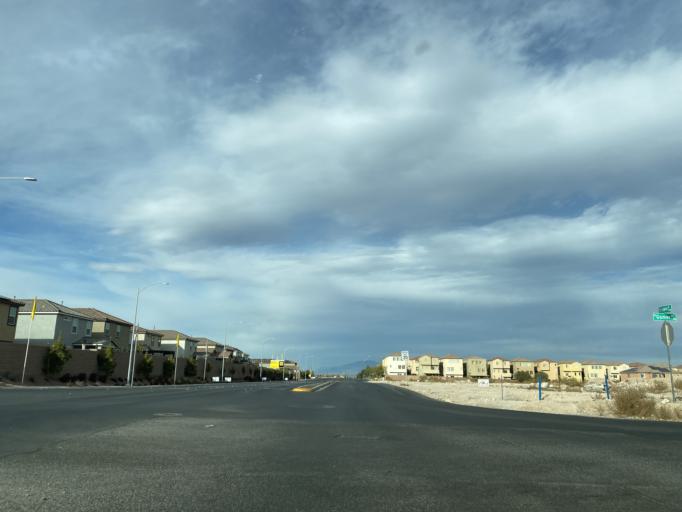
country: US
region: Nevada
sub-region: Clark County
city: Enterprise
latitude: 36.0120
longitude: -115.2982
